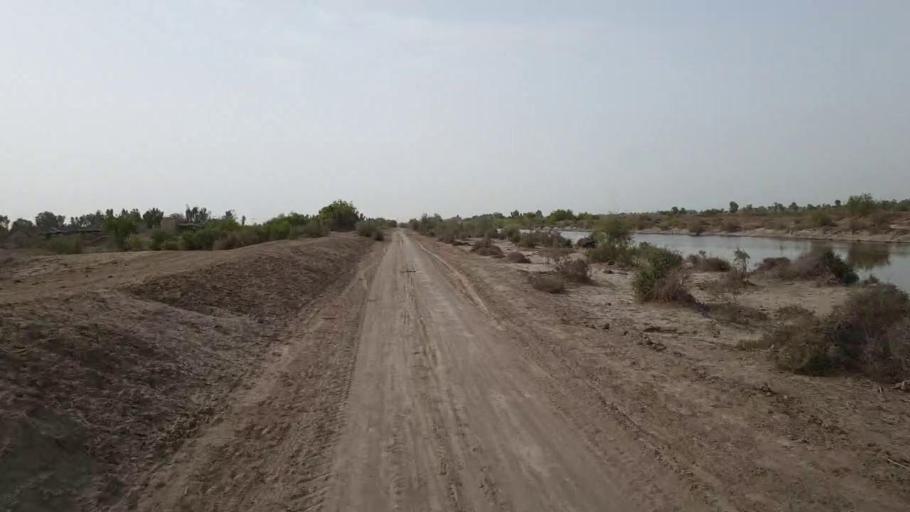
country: PK
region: Sindh
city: Daur
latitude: 26.4198
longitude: 68.1595
